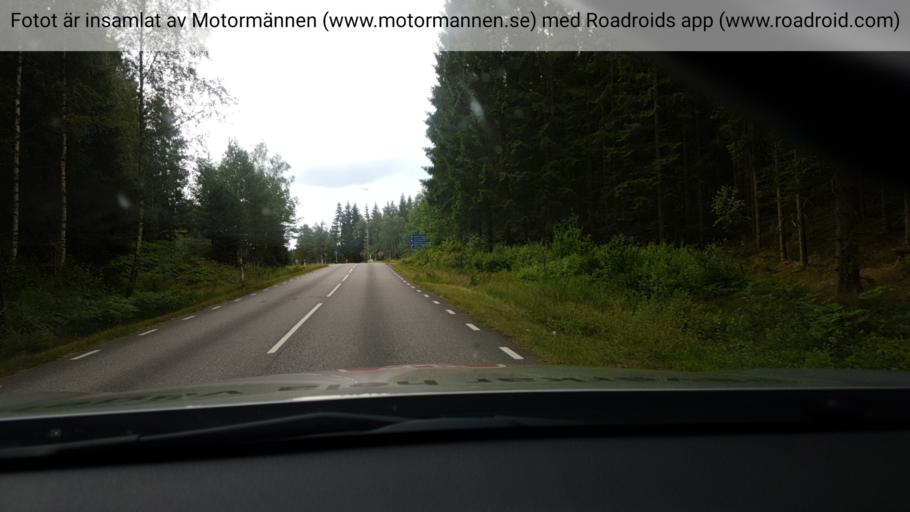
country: SE
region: Vaestra Goetaland
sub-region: Marks Kommun
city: Fritsla
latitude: 57.5410
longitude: 12.8029
